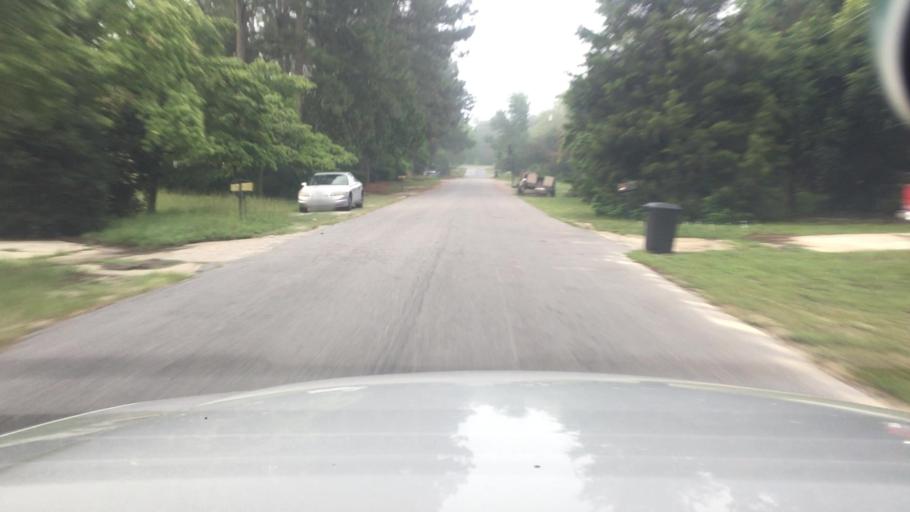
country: US
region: North Carolina
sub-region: Cumberland County
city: Hope Mills
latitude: 35.0193
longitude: -78.9376
